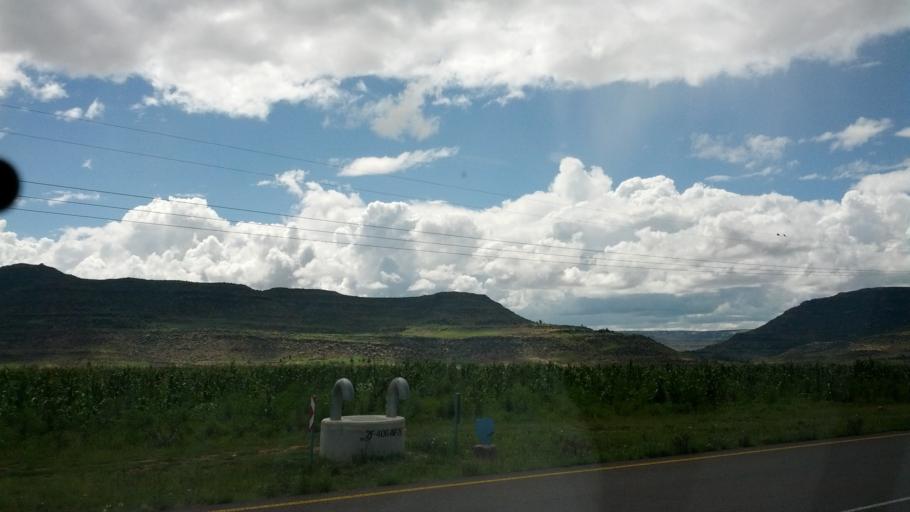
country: LS
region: Maseru
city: Maseru
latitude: -29.5561
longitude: 27.4951
